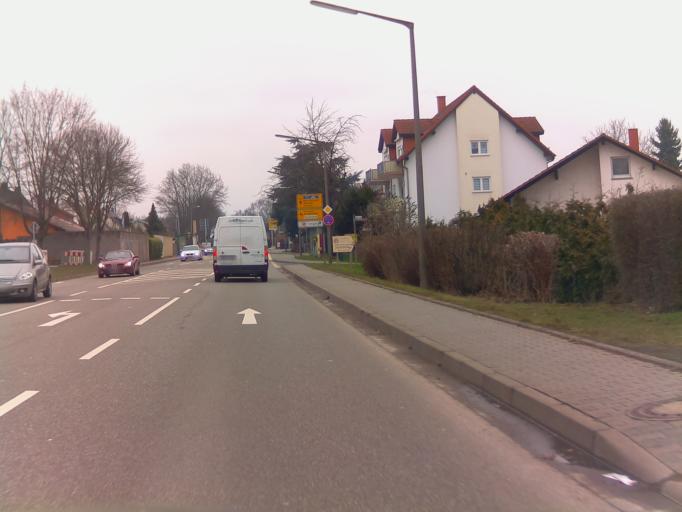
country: DE
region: Rheinland-Pfalz
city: Worrstadt
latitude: 49.8373
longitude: 8.1137
